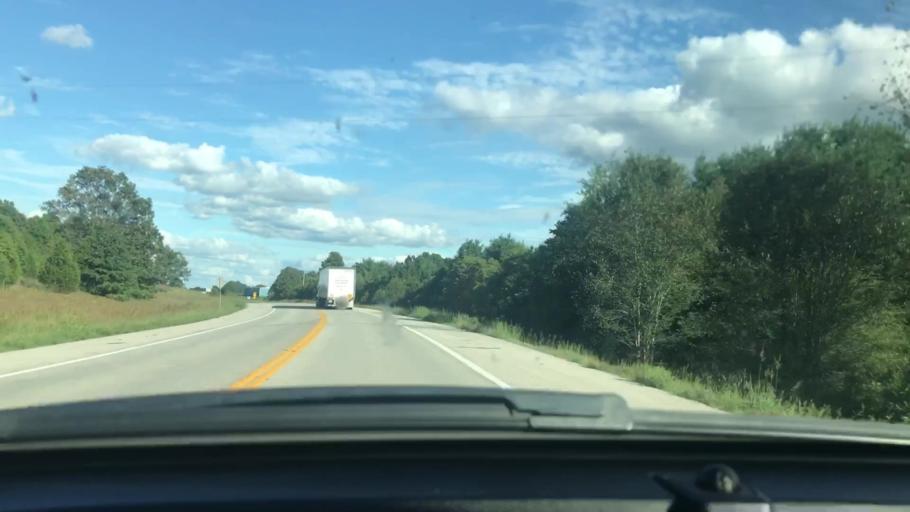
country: US
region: Missouri
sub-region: Oregon County
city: Thayer
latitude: 36.5893
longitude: -91.6400
